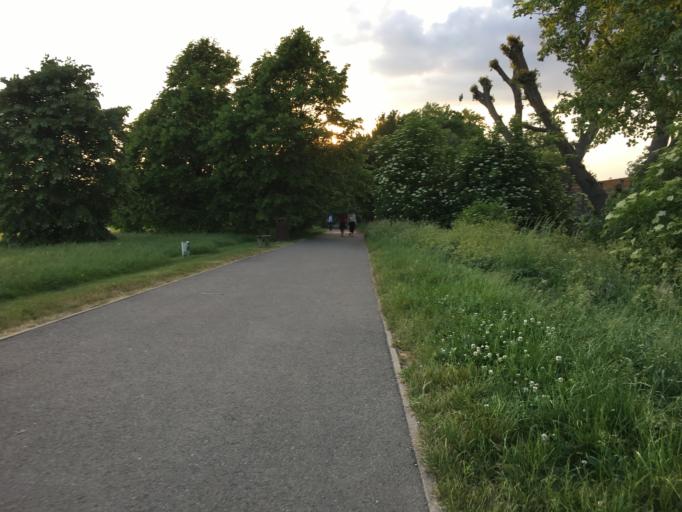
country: GB
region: England
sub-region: Greater London
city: Camden Town
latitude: 51.5339
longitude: -0.1551
